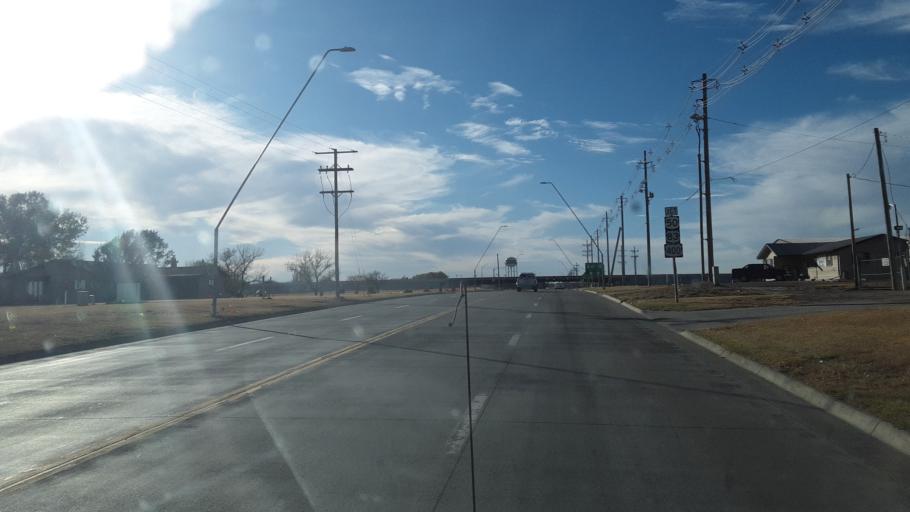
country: US
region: Kansas
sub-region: Finney County
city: Garden City
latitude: 37.9894
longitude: -100.8350
